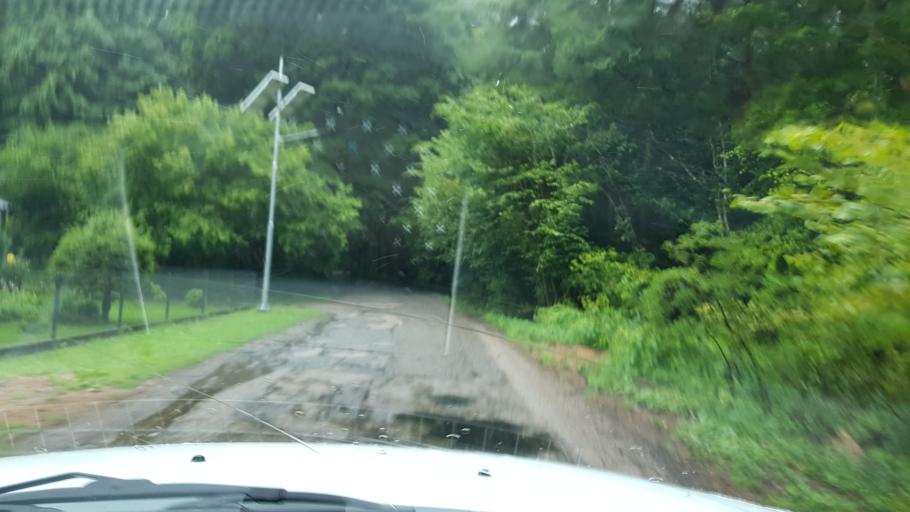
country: PL
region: West Pomeranian Voivodeship
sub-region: Powiat gryficki
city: Brojce
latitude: 53.9559
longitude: 15.4410
